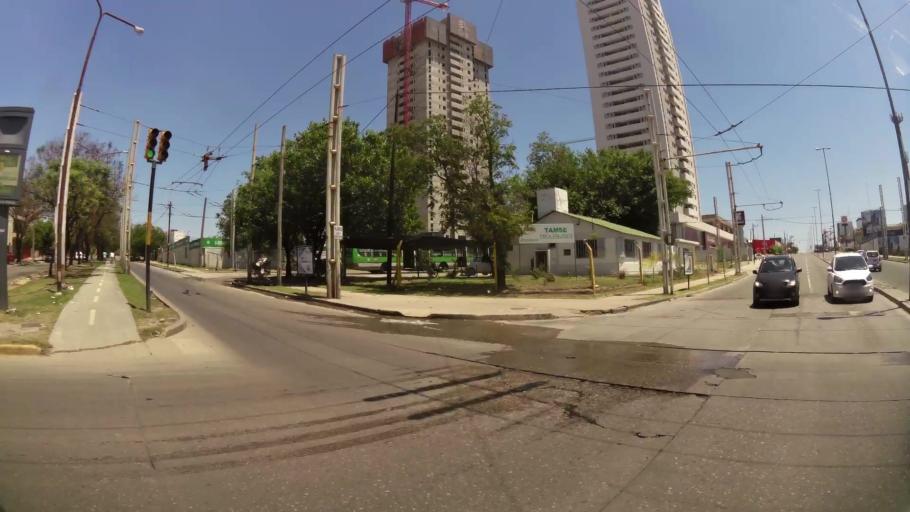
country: AR
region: Cordoba
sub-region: Departamento de Capital
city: Cordoba
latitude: -31.4009
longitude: -64.2253
